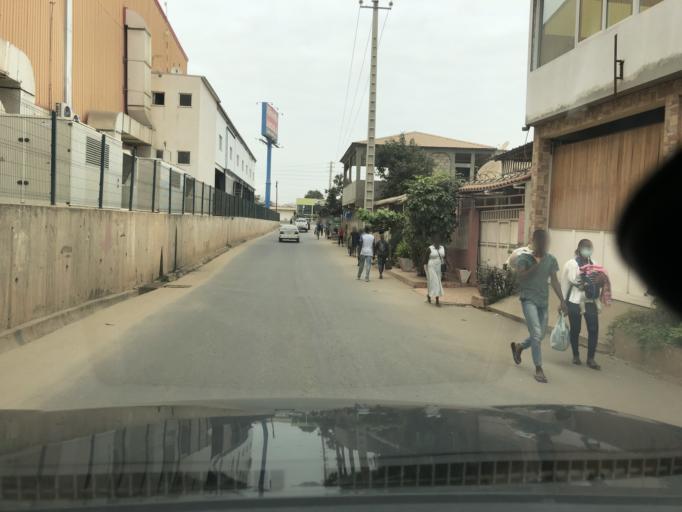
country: AO
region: Luanda
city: Luanda
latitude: -8.9006
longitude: 13.2587
